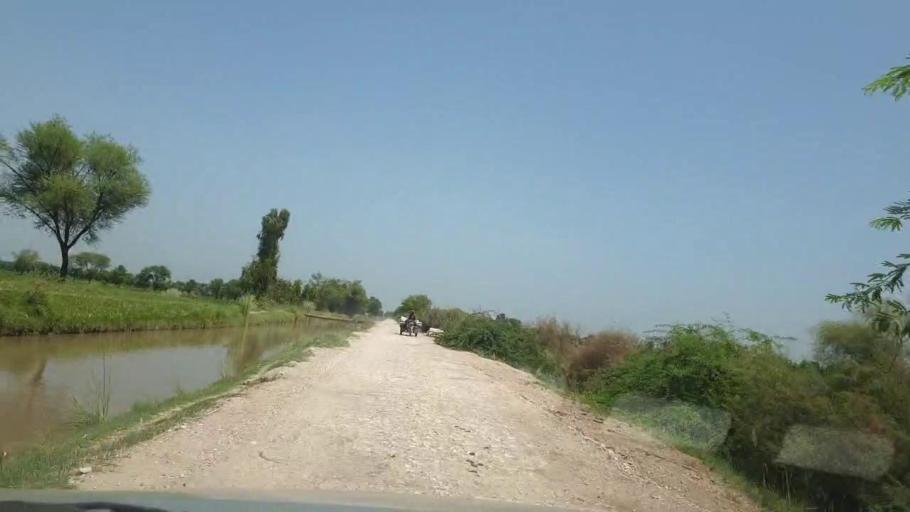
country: PK
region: Sindh
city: Rohri
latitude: 27.6409
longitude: 69.1030
